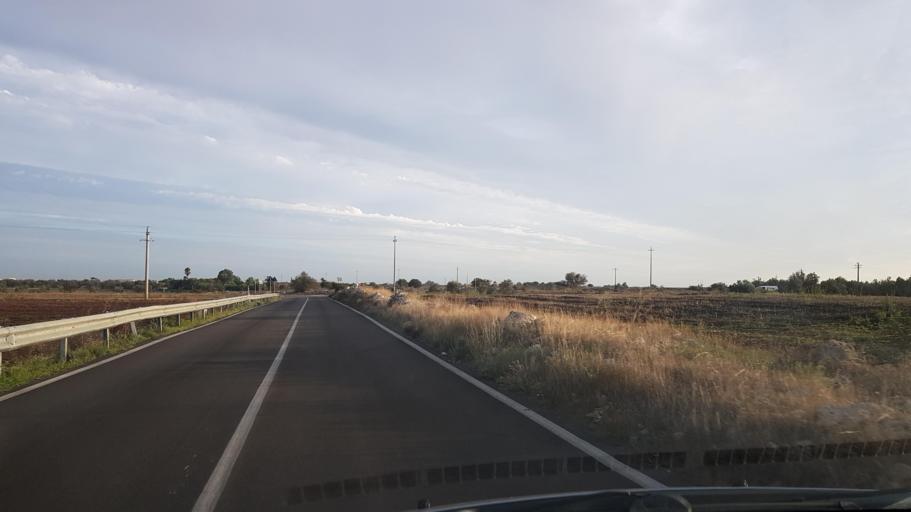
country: IT
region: Apulia
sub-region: Provincia di Lecce
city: Surbo
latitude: 40.4349
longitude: 18.1139
